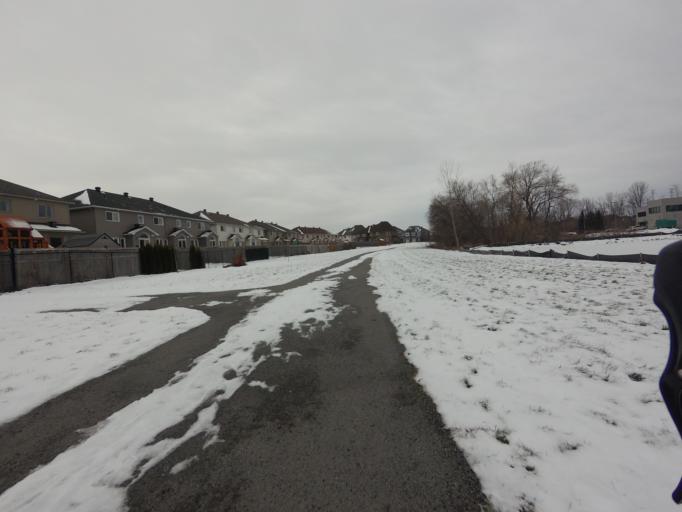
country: CA
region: Ontario
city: Bells Corners
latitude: 45.2801
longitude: -75.8650
